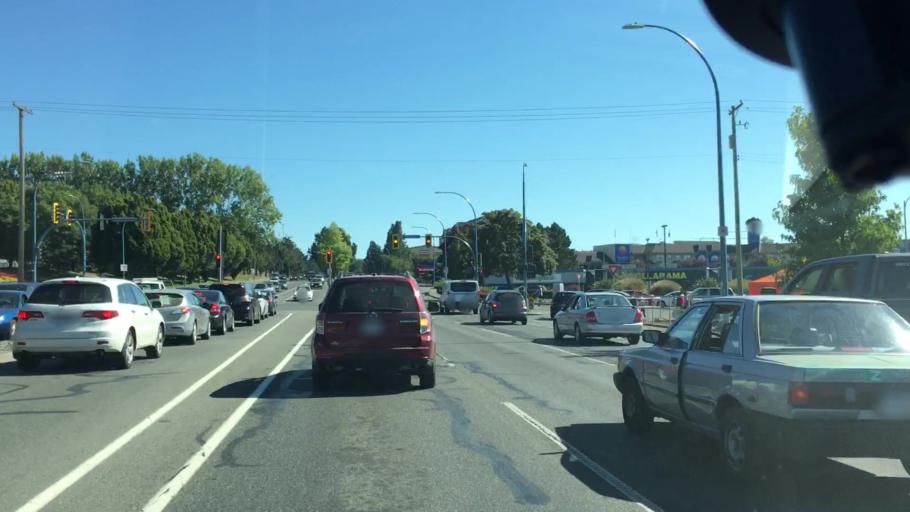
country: CA
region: British Columbia
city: Victoria
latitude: 48.4462
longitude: -123.3669
